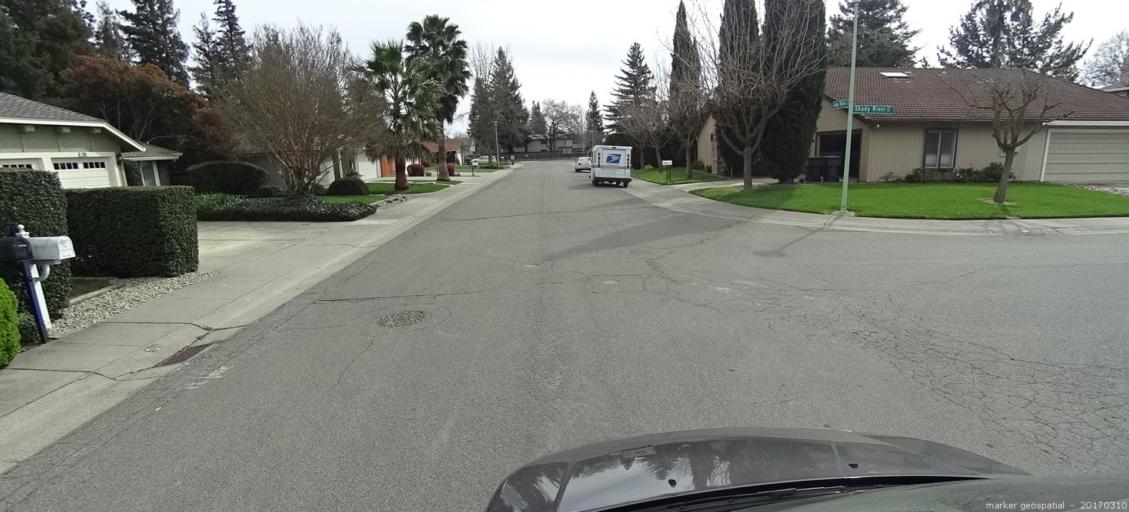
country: US
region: California
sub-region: Sacramento County
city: Parkway
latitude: 38.4935
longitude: -121.5264
